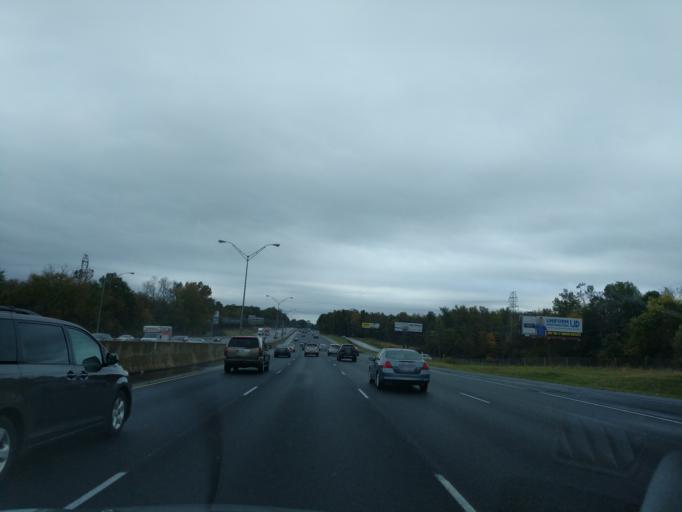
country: US
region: North Carolina
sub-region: Alamance County
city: Elon
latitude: 36.0676
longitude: -79.4964
